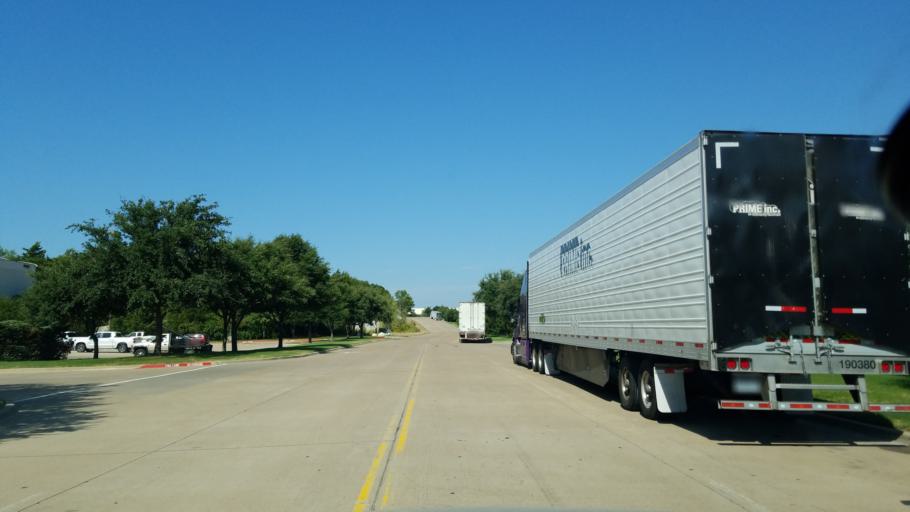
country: US
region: Texas
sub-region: Dallas County
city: Cockrell Hill
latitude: 32.7522
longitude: -96.8868
